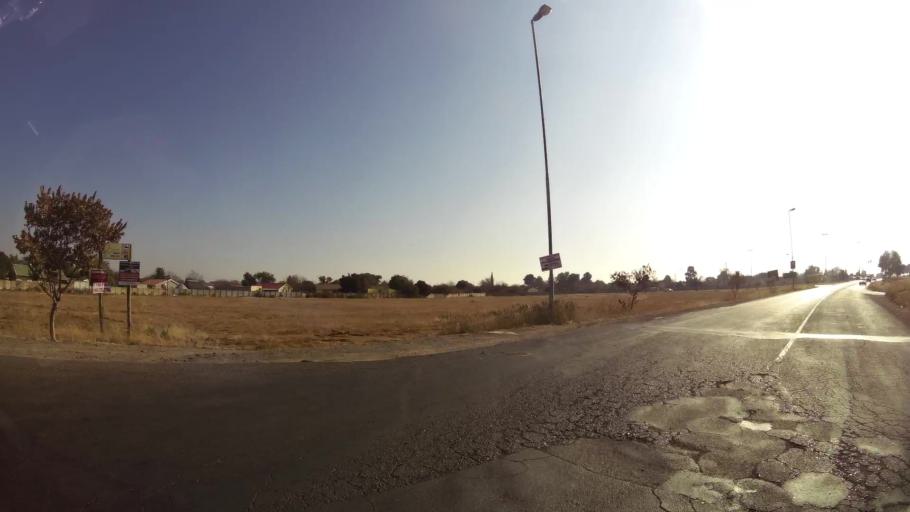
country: ZA
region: Orange Free State
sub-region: Mangaung Metropolitan Municipality
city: Bloemfontein
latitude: -29.1707
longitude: 26.1944
